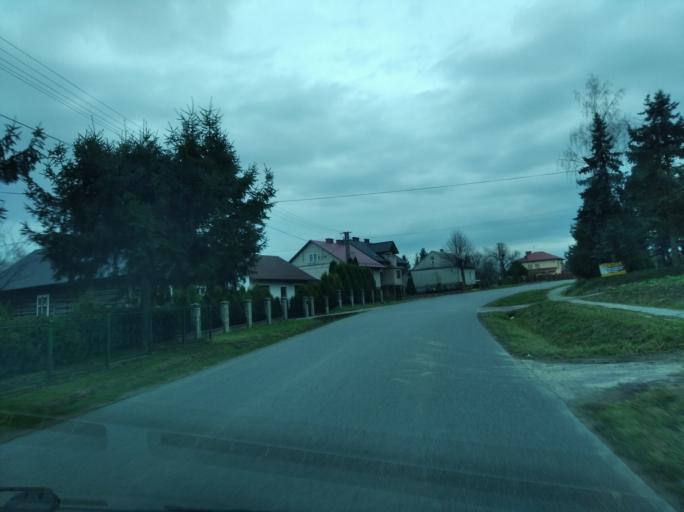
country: PL
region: Subcarpathian Voivodeship
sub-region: Powiat ropczycko-sedziszowski
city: Iwierzyce
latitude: 50.0094
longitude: 21.7553
